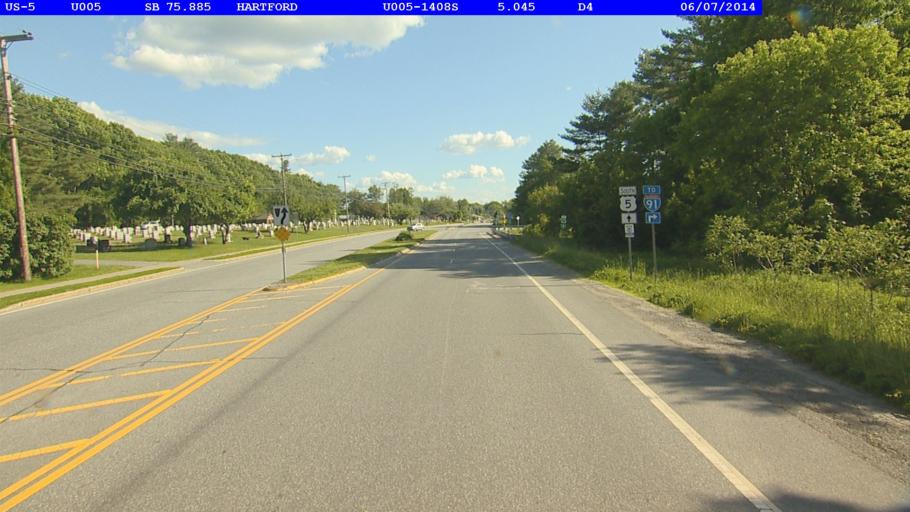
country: US
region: Vermont
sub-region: Windsor County
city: Wilder
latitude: 43.6646
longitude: -72.3129
